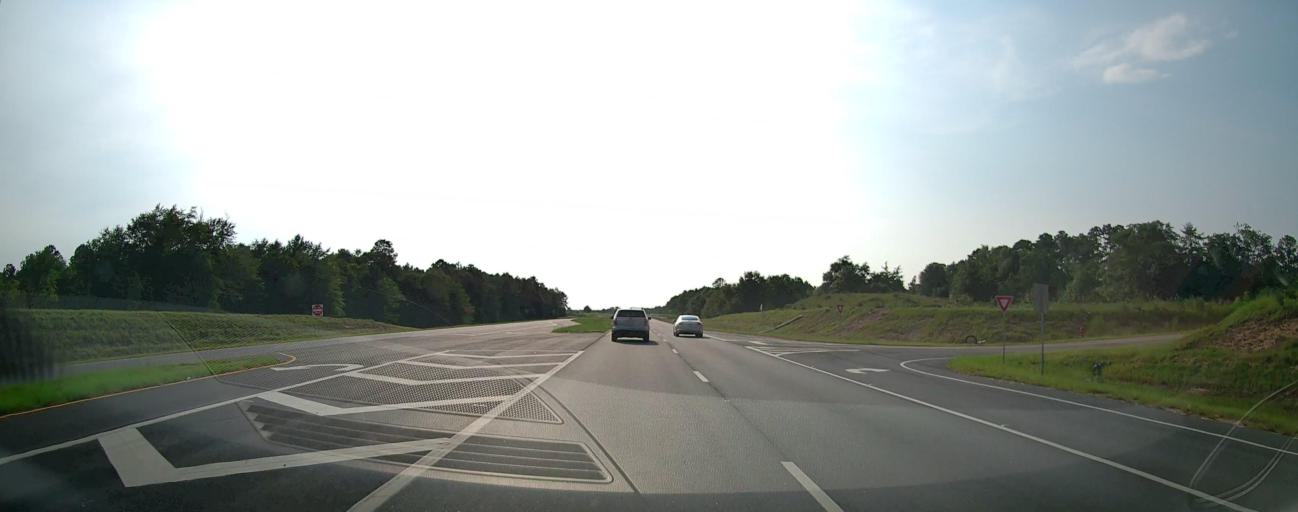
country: US
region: Georgia
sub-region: Taylor County
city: Butler
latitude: 32.5456
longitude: -84.2460
